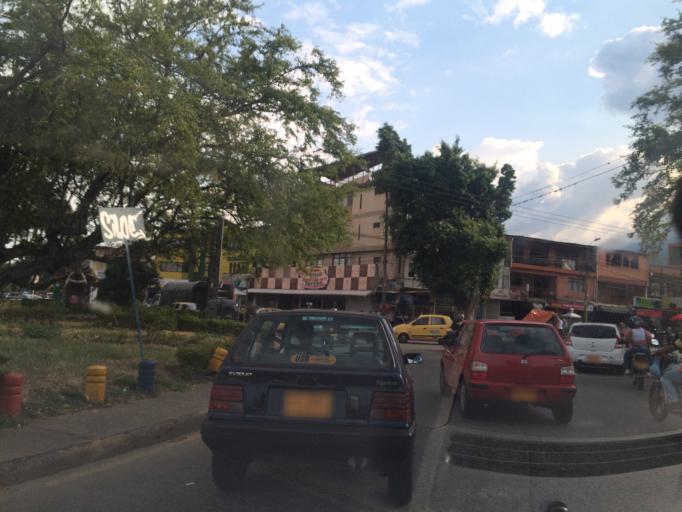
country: CO
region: Valle del Cauca
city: Cali
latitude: 3.4165
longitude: -76.5547
